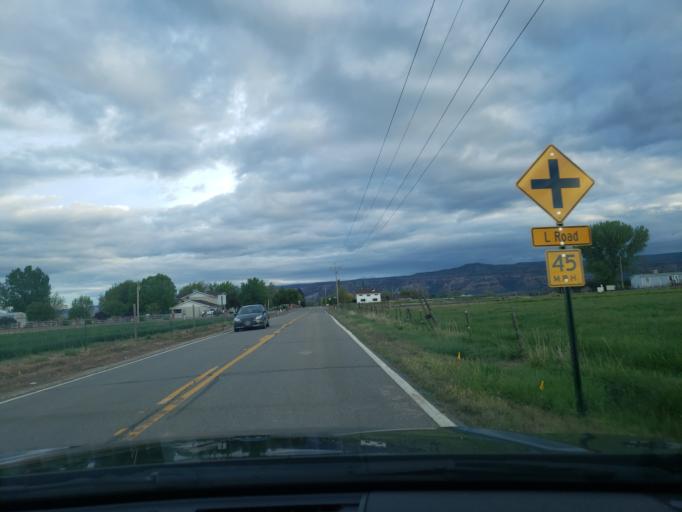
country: US
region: Colorado
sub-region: Mesa County
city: Fruita
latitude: 39.1800
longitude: -108.7013
